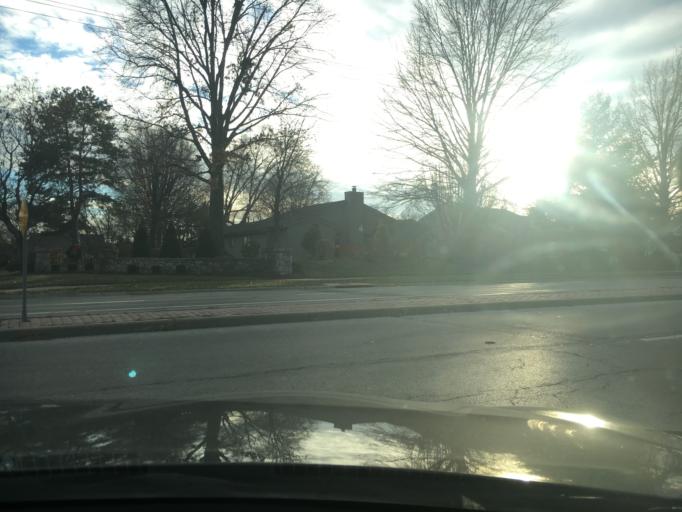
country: US
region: Kansas
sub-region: Johnson County
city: Leawood
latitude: 38.9058
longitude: -94.6100
